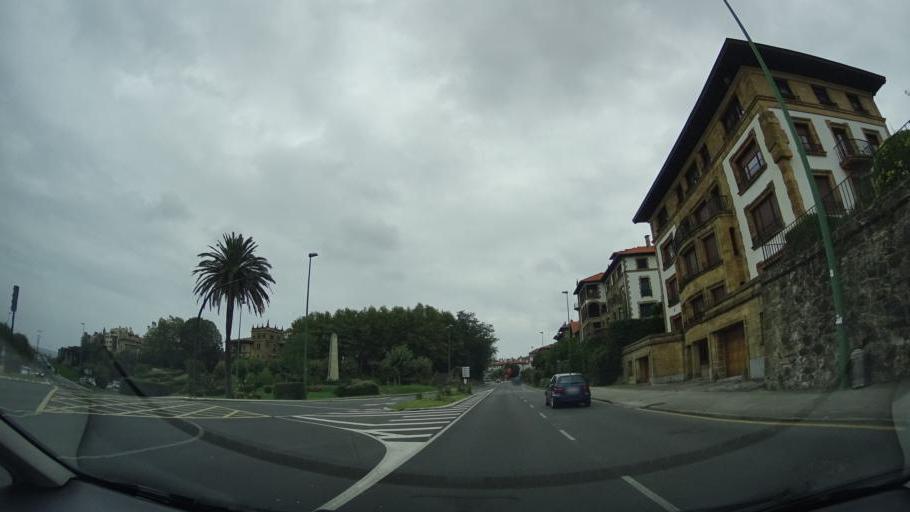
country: ES
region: Basque Country
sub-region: Bizkaia
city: Algorta
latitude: 43.3372
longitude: -3.0094
